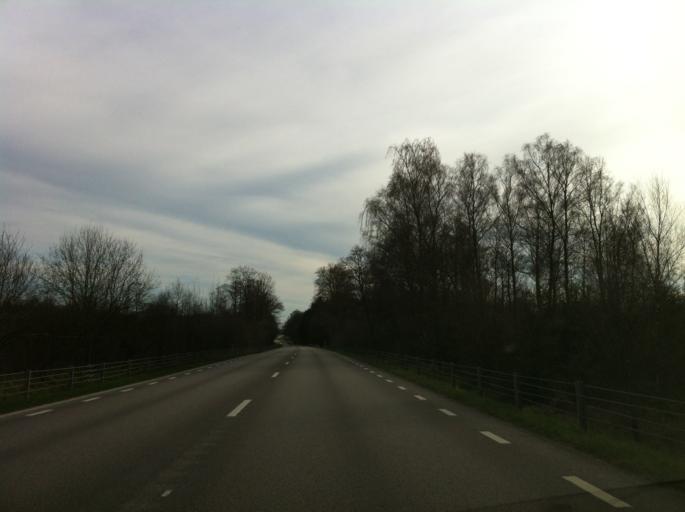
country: SE
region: Skane
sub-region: Bjuvs Kommun
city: Billesholm
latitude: 56.0190
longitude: 12.9605
